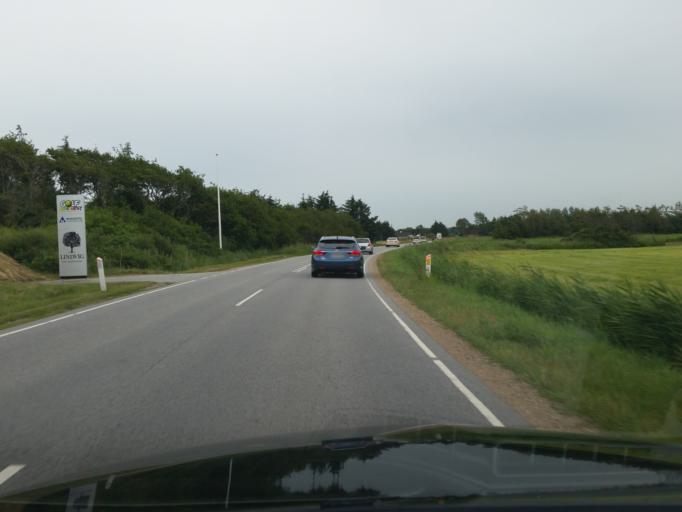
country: DK
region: South Denmark
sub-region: Varde Kommune
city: Oksbol
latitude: 55.8026
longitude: 8.2282
